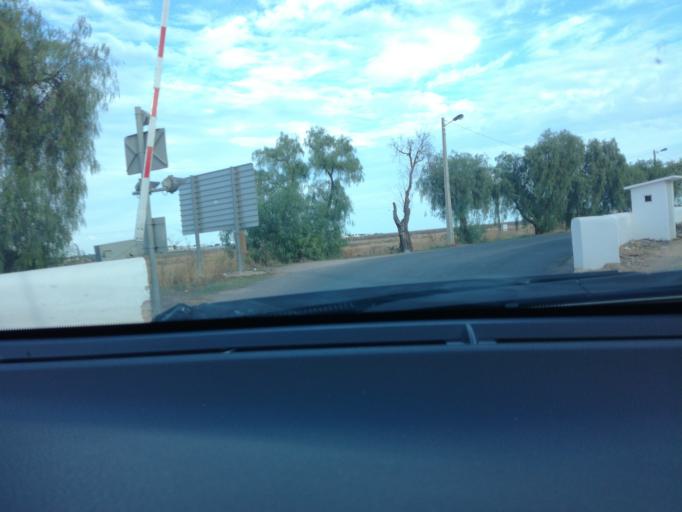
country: PT
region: Faro
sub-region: Olhao
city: Laranjeiro
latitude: 37.0613
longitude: -7.7534
